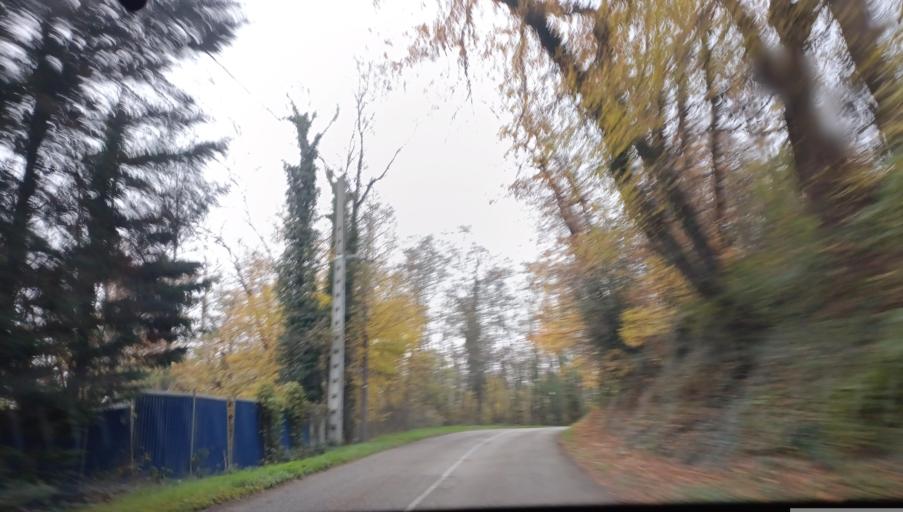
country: FR
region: Rhone-Alpes
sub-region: Departement de l'Isere
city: Serpaize
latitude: 45.5499
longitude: 4.9258
